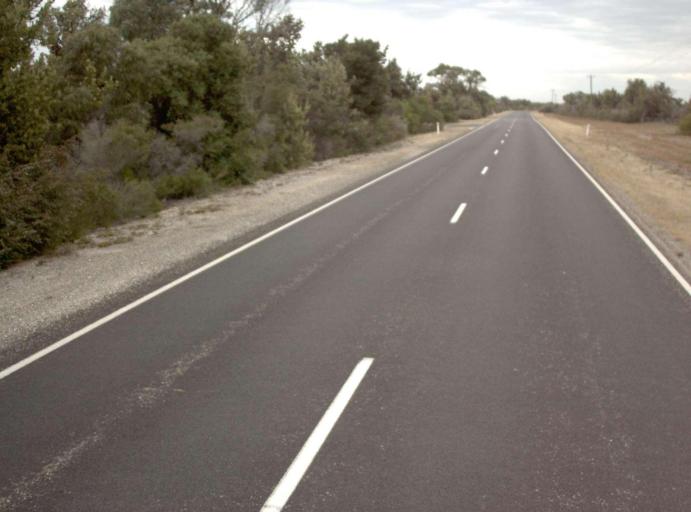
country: AU
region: Victoria
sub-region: Wellington
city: Sale
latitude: -38.1858
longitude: 147.3715
